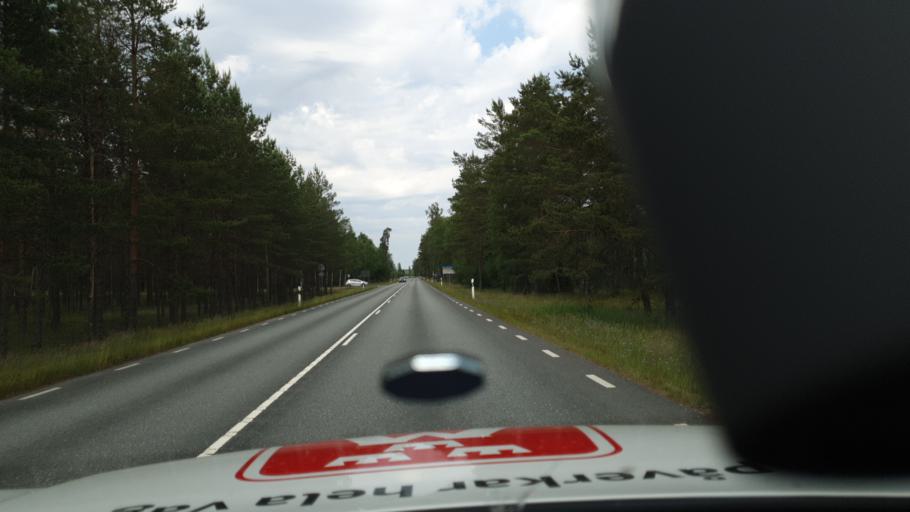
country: SE
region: Joenkoeping
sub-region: Varnamo Kommun
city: Varnamo
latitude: 57.2986
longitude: 14.0820
